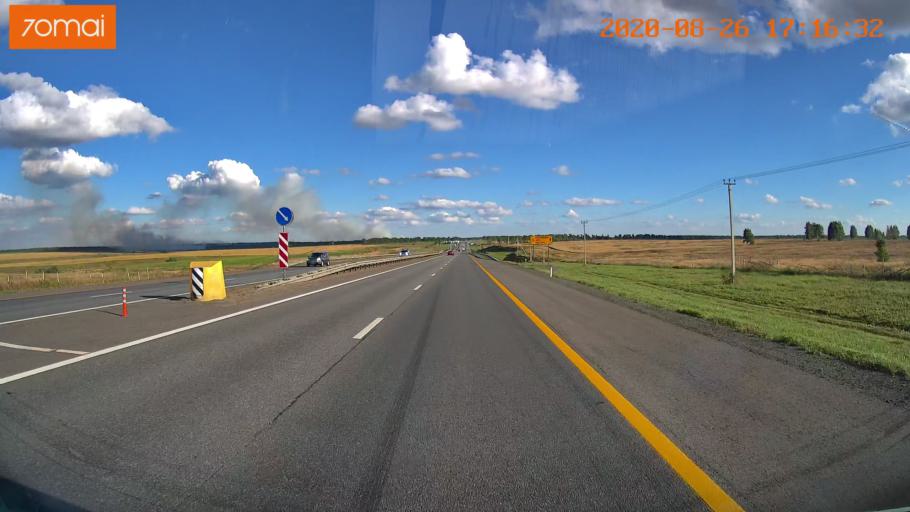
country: RU
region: Tula
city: Volovo
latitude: 53.6352
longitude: 38.0732
